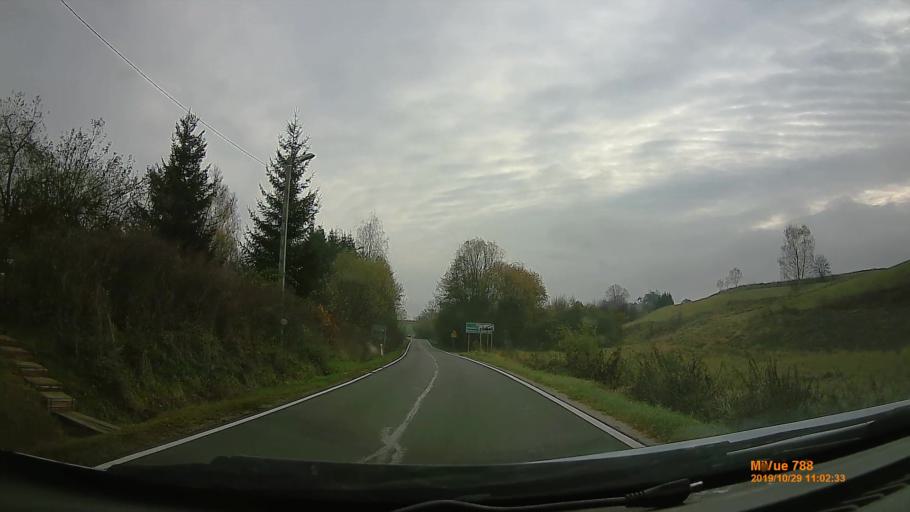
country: PL
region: Lower Silesian Voivodeship
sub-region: Powiat klodzki
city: Radkow
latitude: 50.4882
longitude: 16.4608
